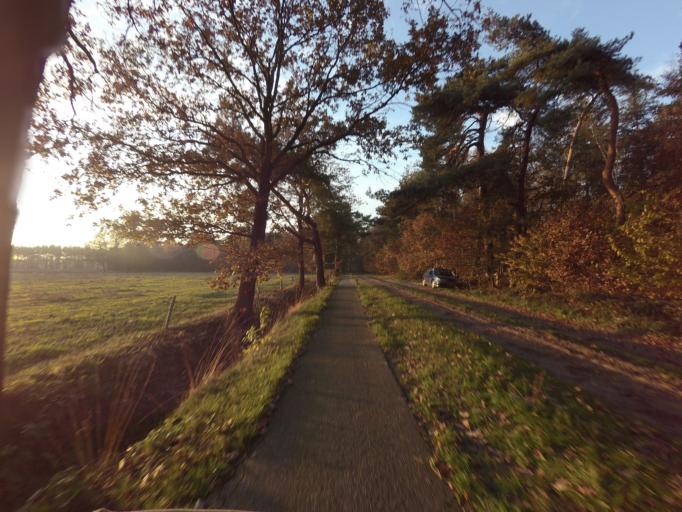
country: NL
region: North Brabant
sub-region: Gemeente Breda
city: Breda
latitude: 51.5228
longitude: 4.8082
